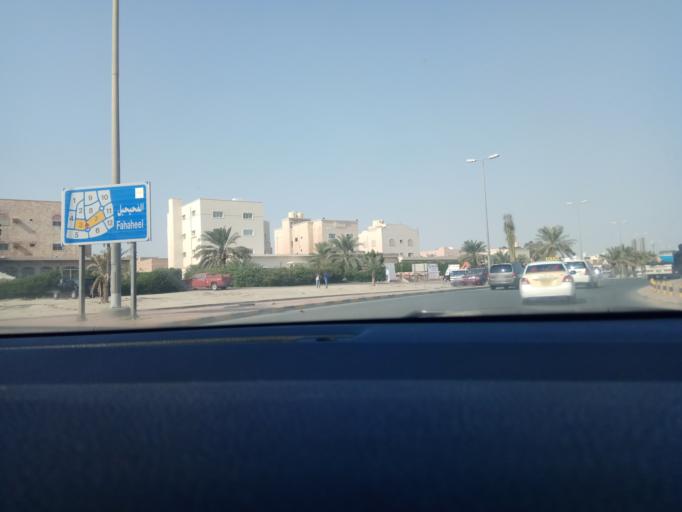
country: KW
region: Al Ahmadi
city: Al Fahahil
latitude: 29.0746
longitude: 48.1253
